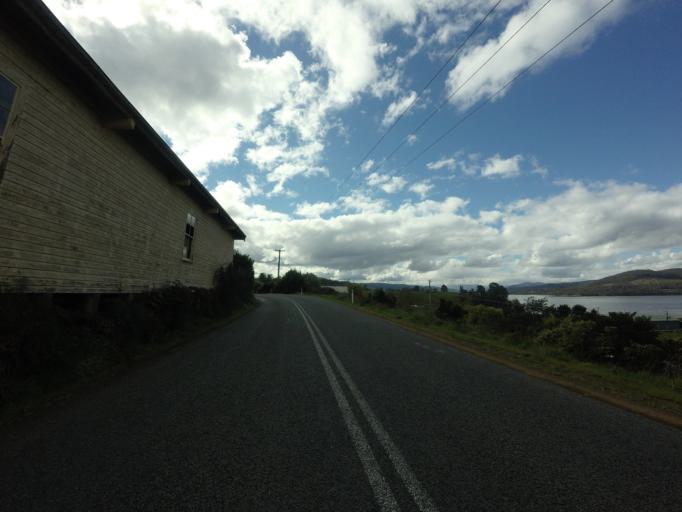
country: AU
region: Tasmania
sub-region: Huon Valley
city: Geeveston
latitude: -43.2059
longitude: 146.9693
